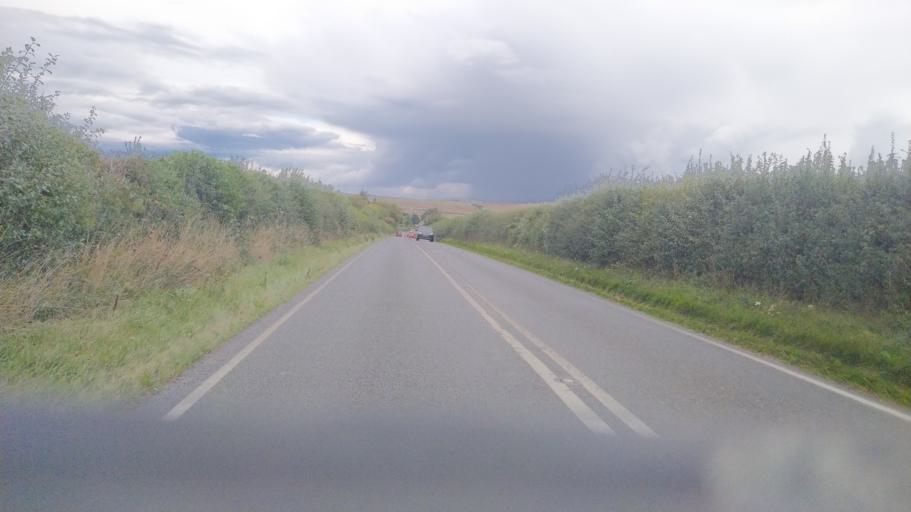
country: GB
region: England
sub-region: Wiltshire
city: Bower Chalke
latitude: 50.9315
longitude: -2.0177
